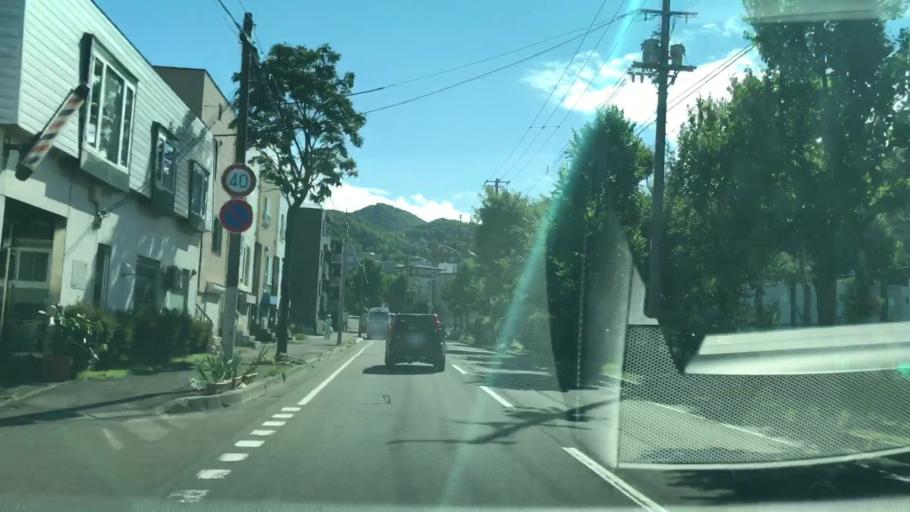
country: JP
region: Hokkaido
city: Sapporo
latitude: 43.0614
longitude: 141.3013
